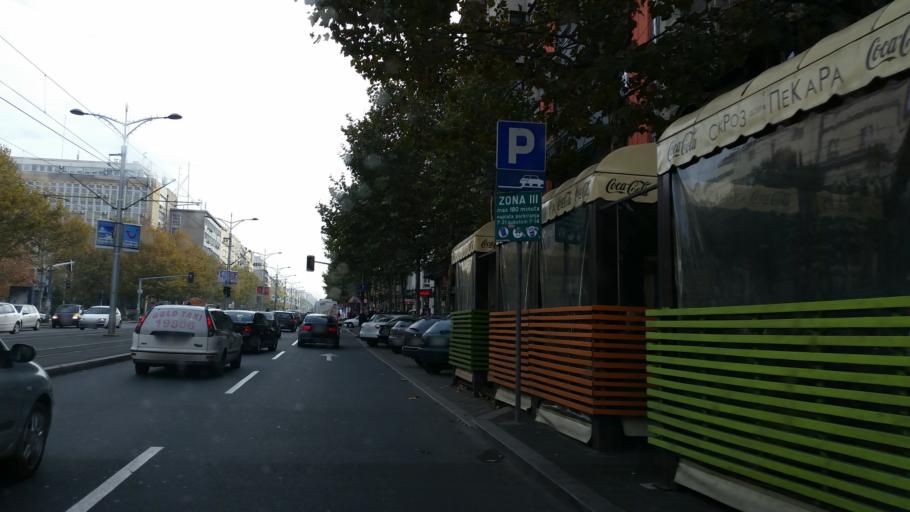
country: RS
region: Central Serbia
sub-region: Belgrade
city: Vracar
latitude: 44.8037
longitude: 20.4792
